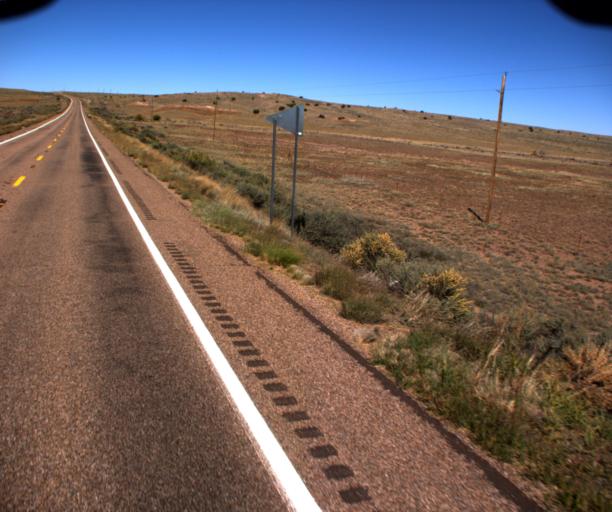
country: US
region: Arizona
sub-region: Apache County
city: Saint Johns
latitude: 34.5227
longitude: -109.4544
